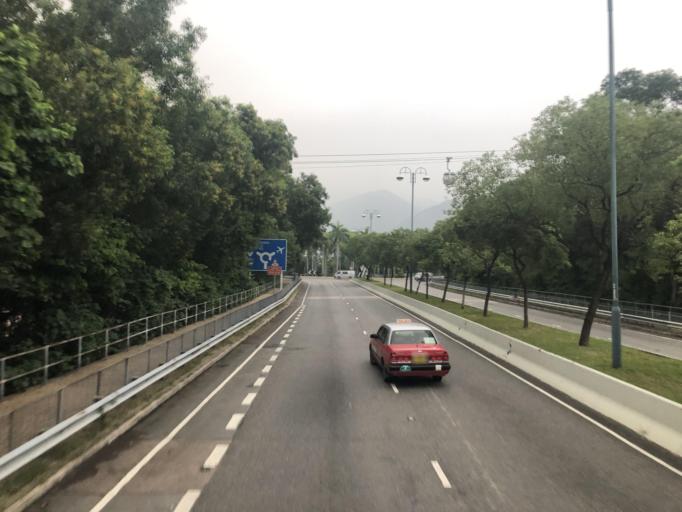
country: HK
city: Tai O
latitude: 22.2912
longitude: 113.9383
